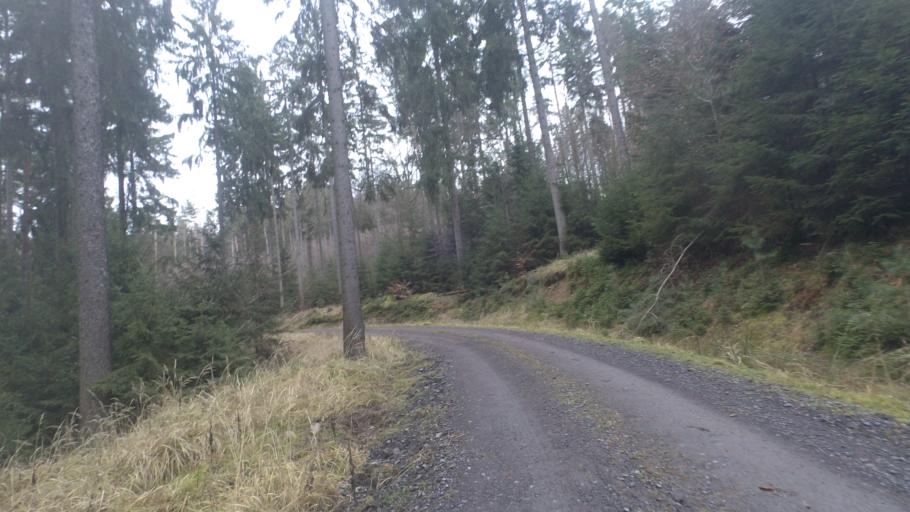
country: DE
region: Thuringia
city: Herschdorf
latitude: 50.7010
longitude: 11.4970
